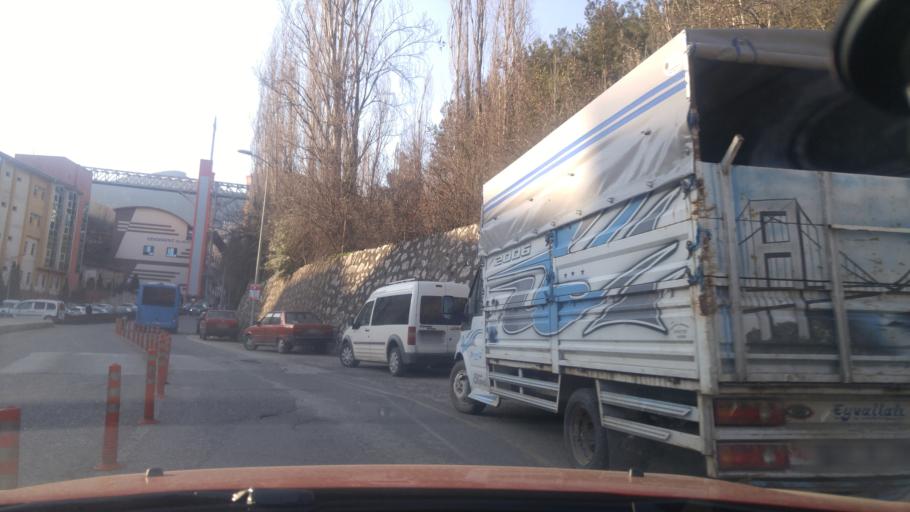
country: TR
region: Karabuk
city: Karabuk
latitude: 41.1983
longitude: 32.6176
